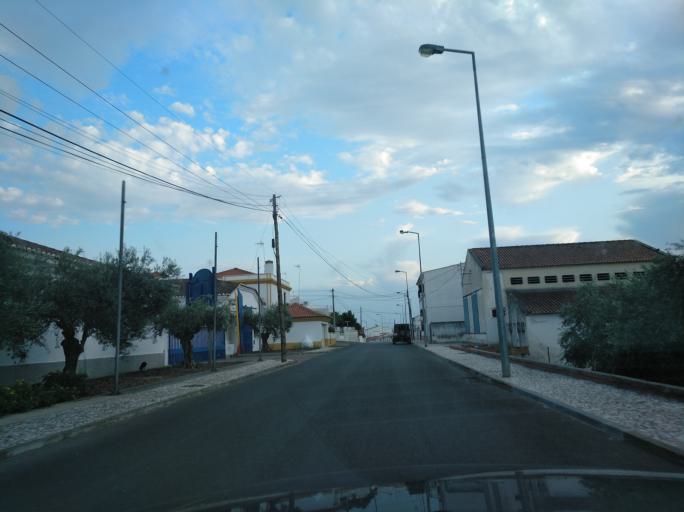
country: PT
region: Portalegre
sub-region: Campo Maior
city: Campo Maior
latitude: 39.0192
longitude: -7.0679
